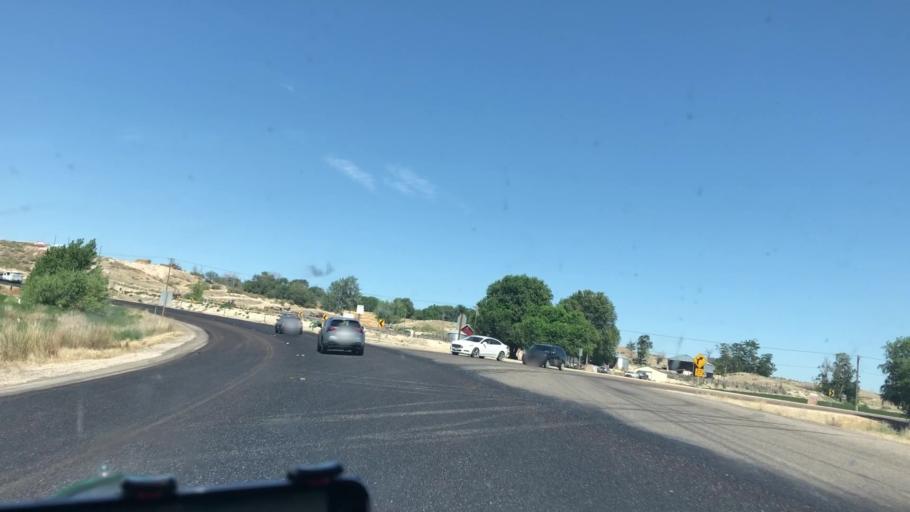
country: US
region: Idaho
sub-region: Owyhee County
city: Marsing
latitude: 43.5502
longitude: -116.7940
